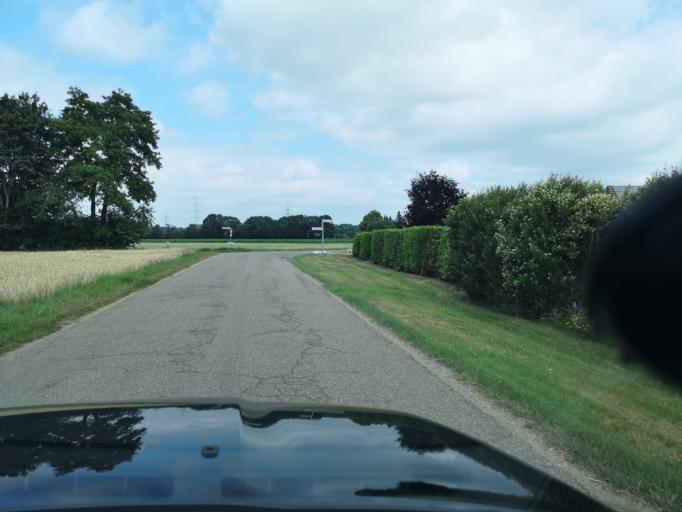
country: DE
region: North Rhine-Westphalia
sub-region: Regierungsbezirk Dusseldorf
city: Wesel
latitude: 51.6910
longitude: 6.6349
